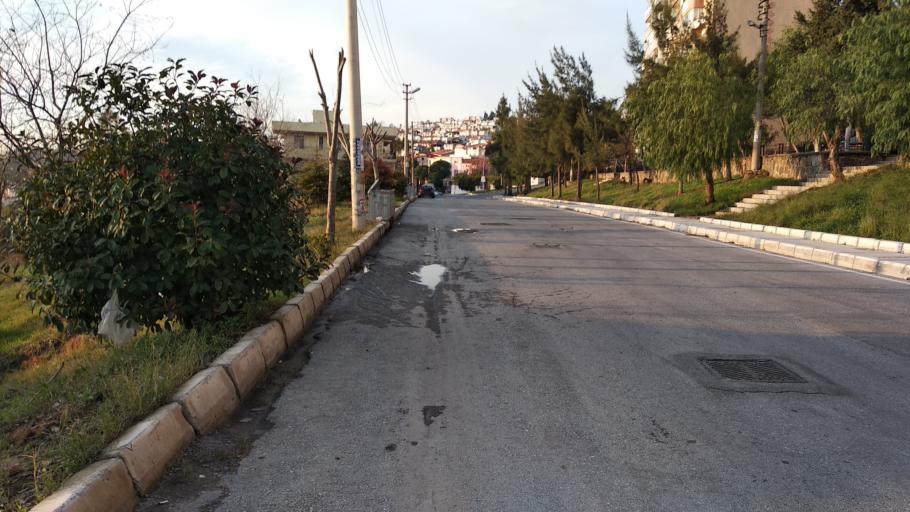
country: TR
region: Izmir
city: Karsiyaka
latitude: 38.4949
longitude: 27.0856
